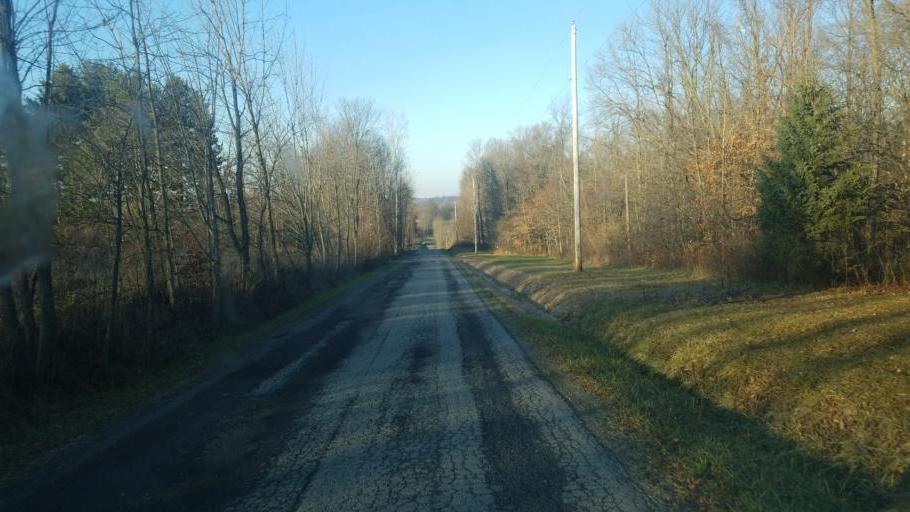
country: US
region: Ohio
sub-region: Richland County
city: Lexington
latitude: 40.6958
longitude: -82.6461
